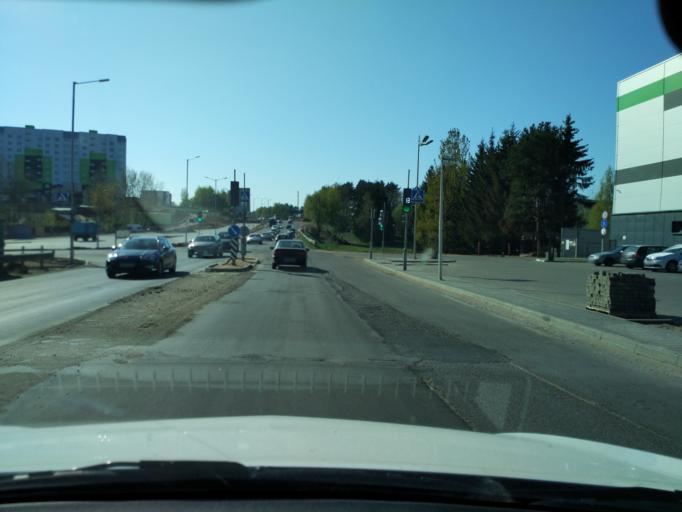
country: BY
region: Minsk
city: Borovlyany
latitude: 53.9641
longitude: 27.6729
